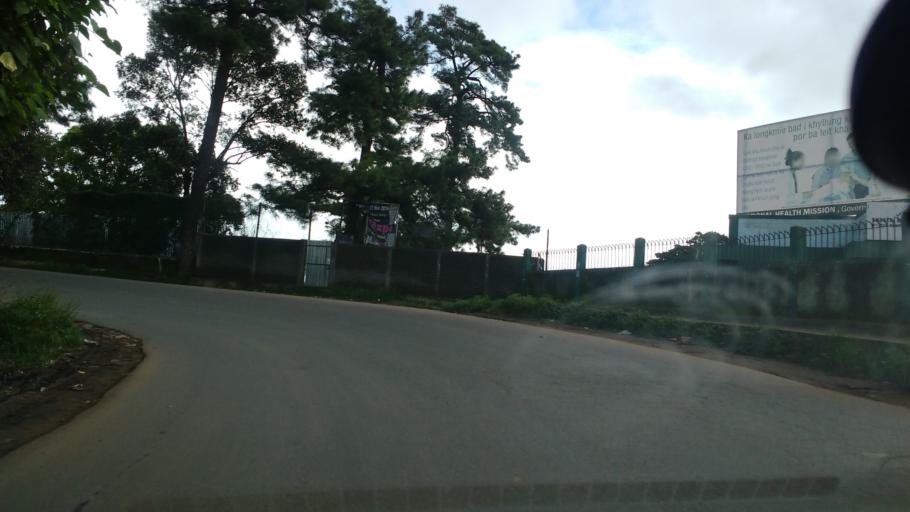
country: IN
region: Meghalaya
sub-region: East Khasi Hills
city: Shillong
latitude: 25.5674
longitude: 91.8568
